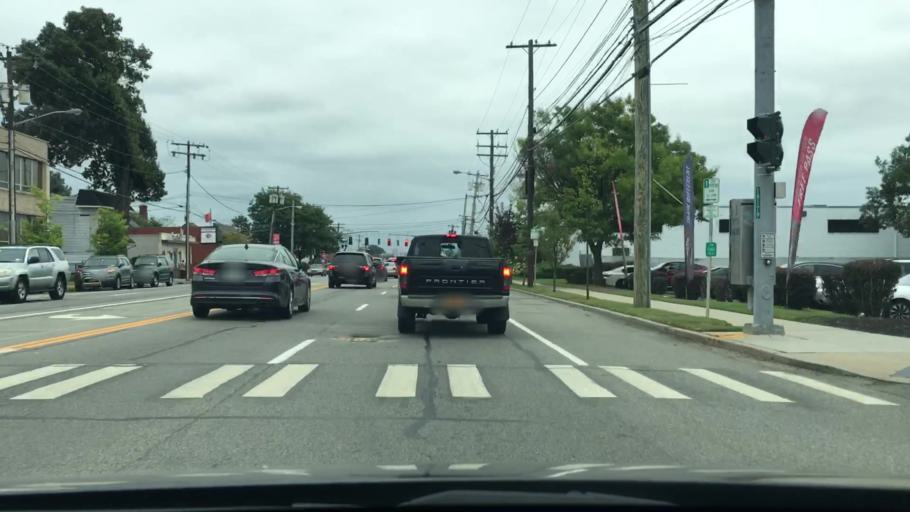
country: US
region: New York
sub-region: Nassau County
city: New Hyde Park
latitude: 40.7353
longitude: -73.6747
